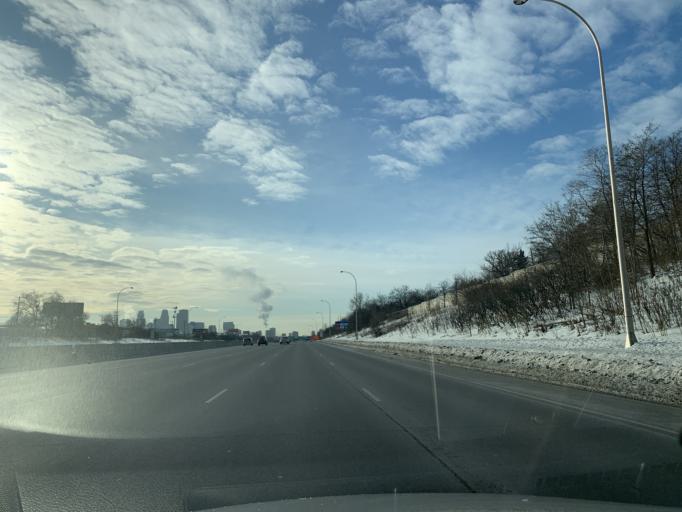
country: US
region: Minnesota
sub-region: Anoka County
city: Columbia Heights
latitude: 45.0124
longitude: -93.2828
